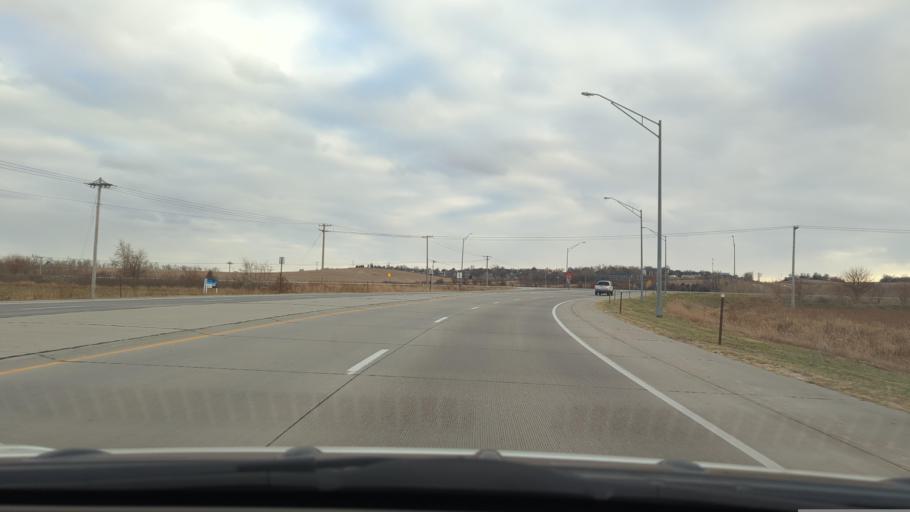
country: US
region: Nebraska
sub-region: Sarpy County
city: Offutt Air Force Base
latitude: 41.1051
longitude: -95.9267
